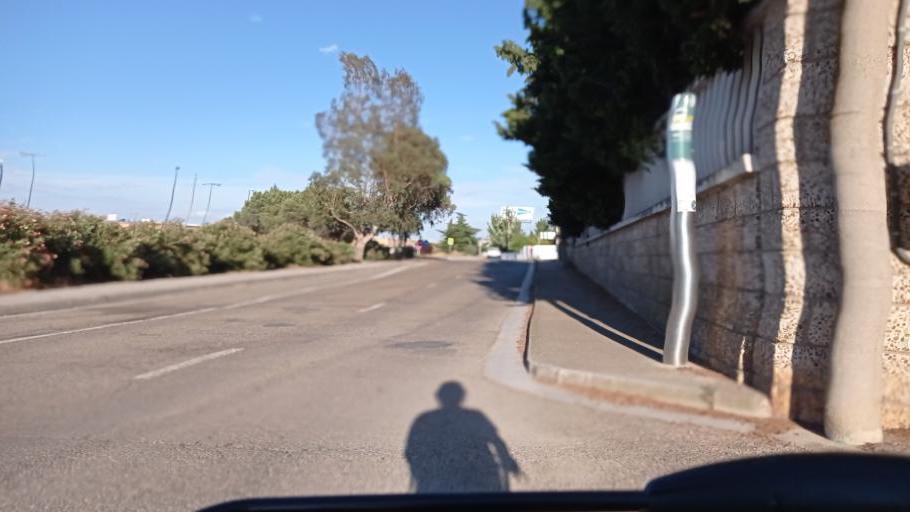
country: ES
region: Aragon
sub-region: Provincia de Zaragoza
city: Oliver-Valdefierro, Oliver, Valdefierro
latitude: 41.6729
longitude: -0.9525
